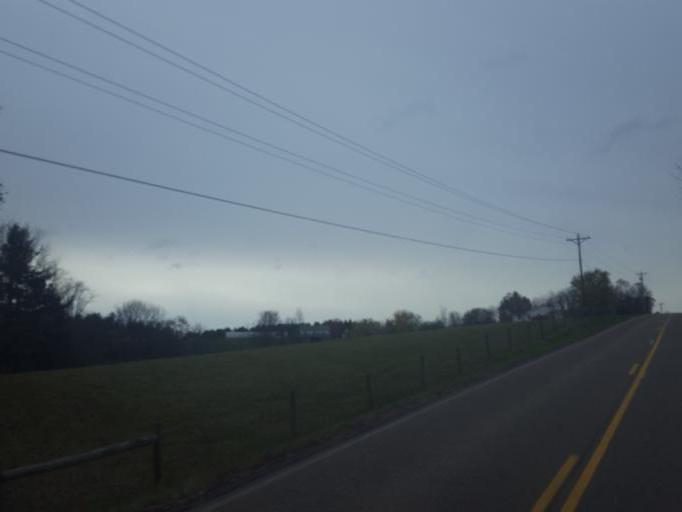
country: US
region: Ohio
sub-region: Knox County
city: Oak Hill
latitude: 40.4452
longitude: -82.1347
